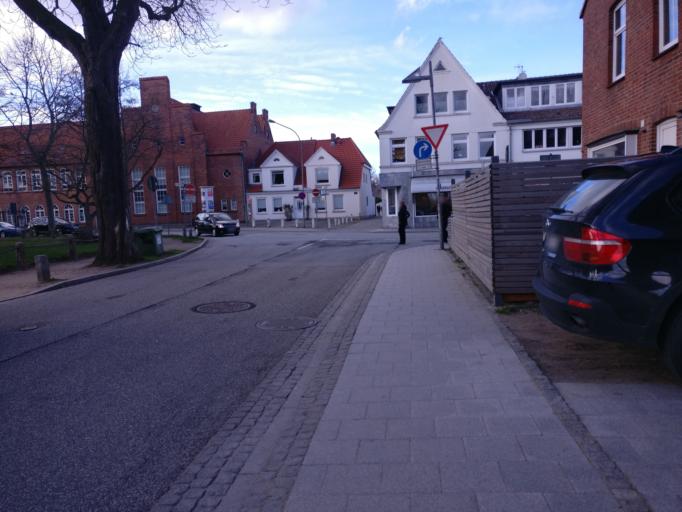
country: DE
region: Schleswig-Holstein
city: Travemuende
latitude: 53.9568
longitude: 10.8660
